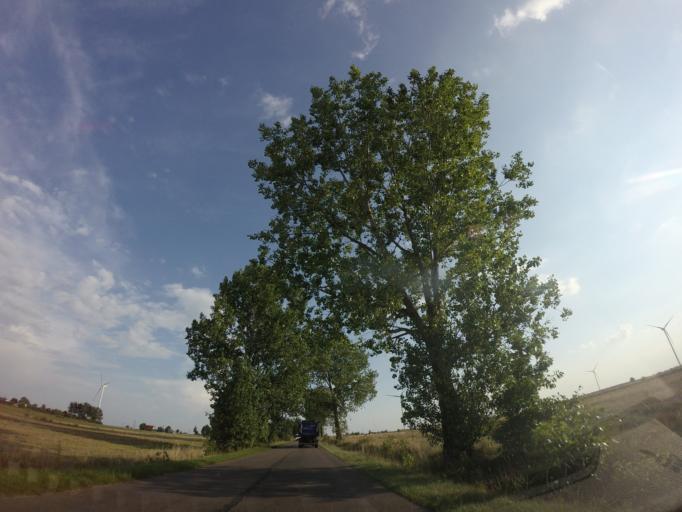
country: PL
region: Lublin Voivodeship
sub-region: Powiat lubartowski
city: Michow
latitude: 51.5100
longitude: 22.3092
